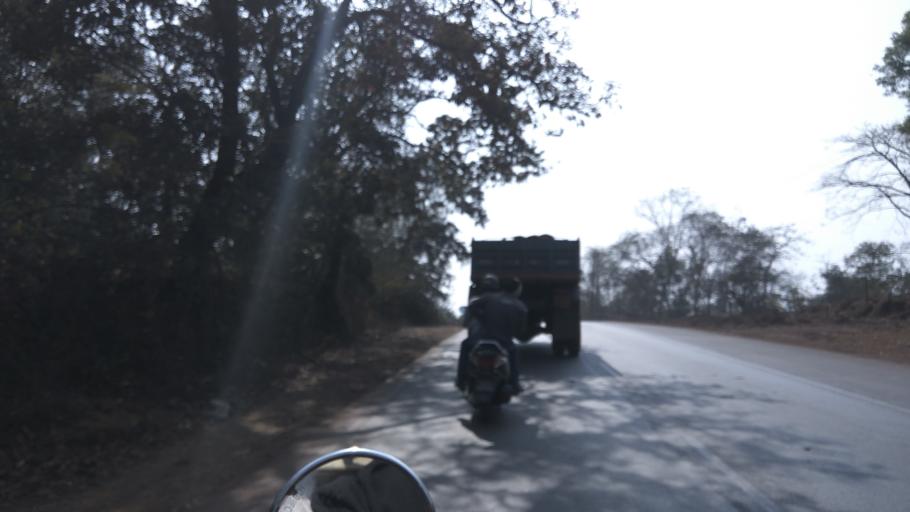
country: IN
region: Goa
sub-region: North Goa
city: Palle
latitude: 15.4066
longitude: 74.0915
